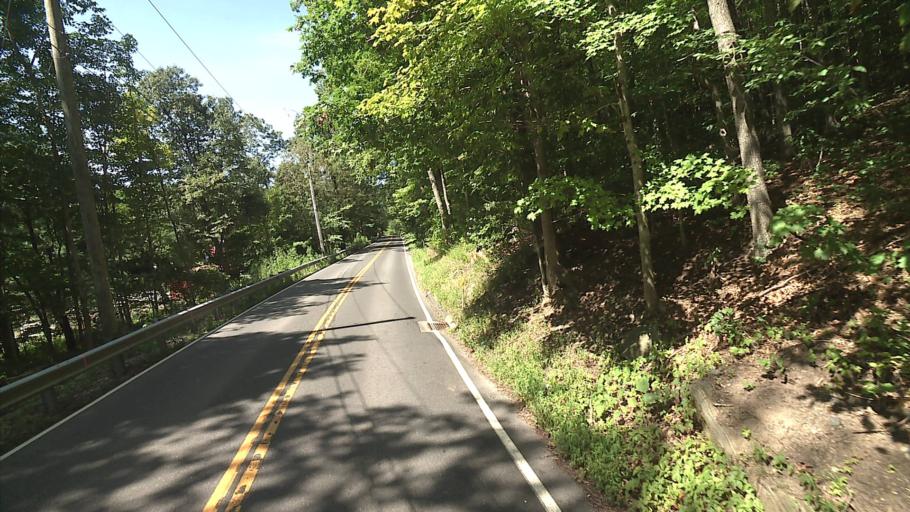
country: US
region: Connecticut
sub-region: New Haven County
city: Oxford
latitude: 41.4507
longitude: -73.1634
